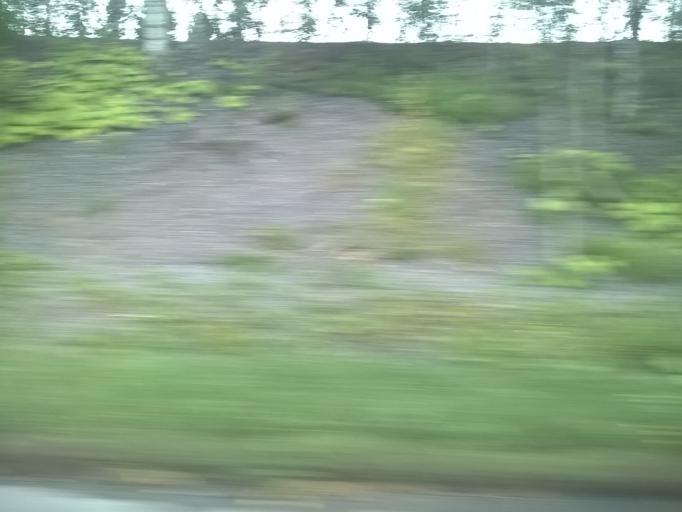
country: FI
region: Pirkanmaa
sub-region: Tampere
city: Tampere
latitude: 61.5047
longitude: 23.7983
